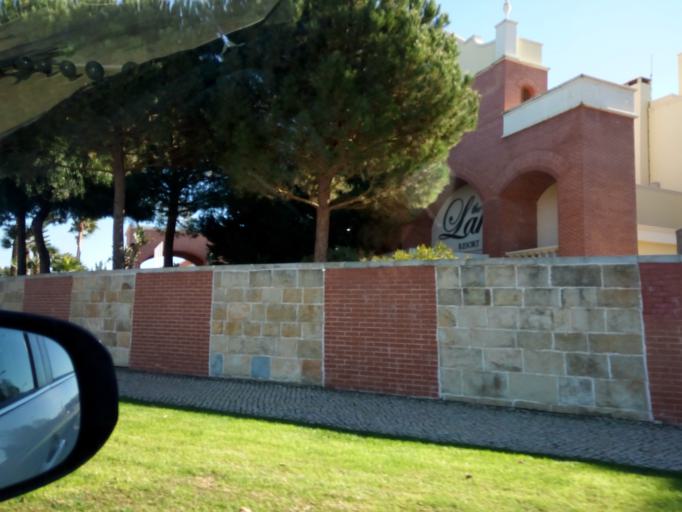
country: PT
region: Faro
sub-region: Loule
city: Vilamoura
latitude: 37.0790
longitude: -8.1273
